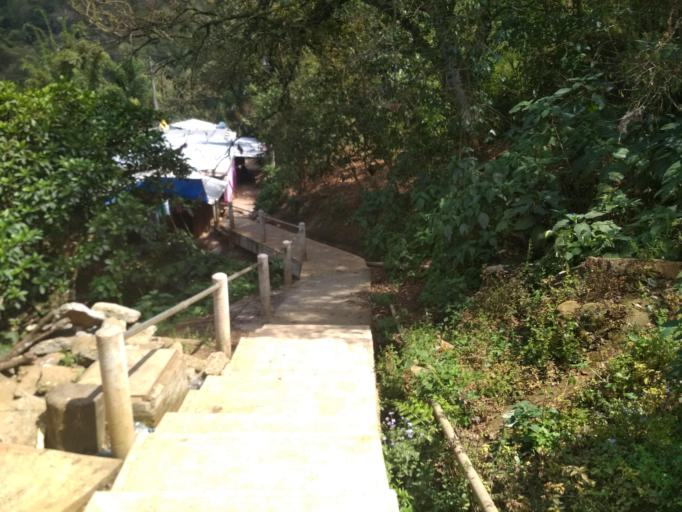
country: MX
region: Veracruz
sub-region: Tlilapan
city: Tonalixco
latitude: 18.7851
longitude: -97.0868
